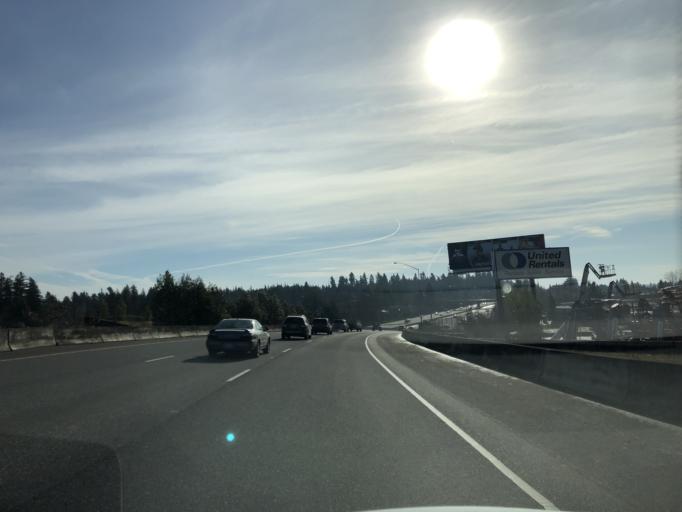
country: US
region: Oregon
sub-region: Washington County
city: Durham
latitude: 45.4200
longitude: -122.7452
